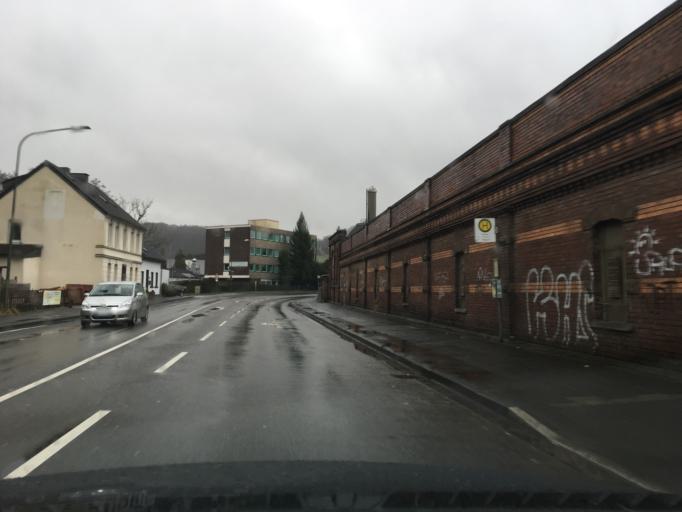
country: DE
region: North Rhine-Westphalia
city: Hattingen
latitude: 51.3699
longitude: 7.1382
